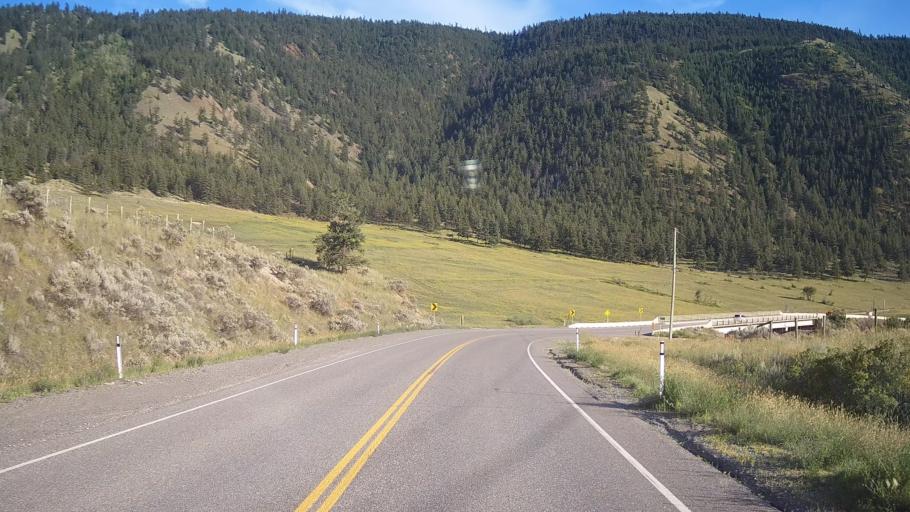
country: CA
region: British Columbia
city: Lillooet
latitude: 50.8735
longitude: -121.8316
